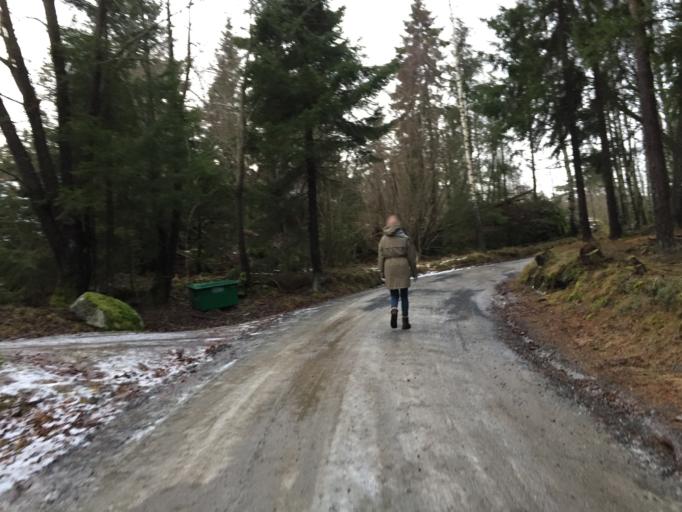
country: NO
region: Ostfold
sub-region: Moss
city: Moss
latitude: 59.4882
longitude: 10.6687
